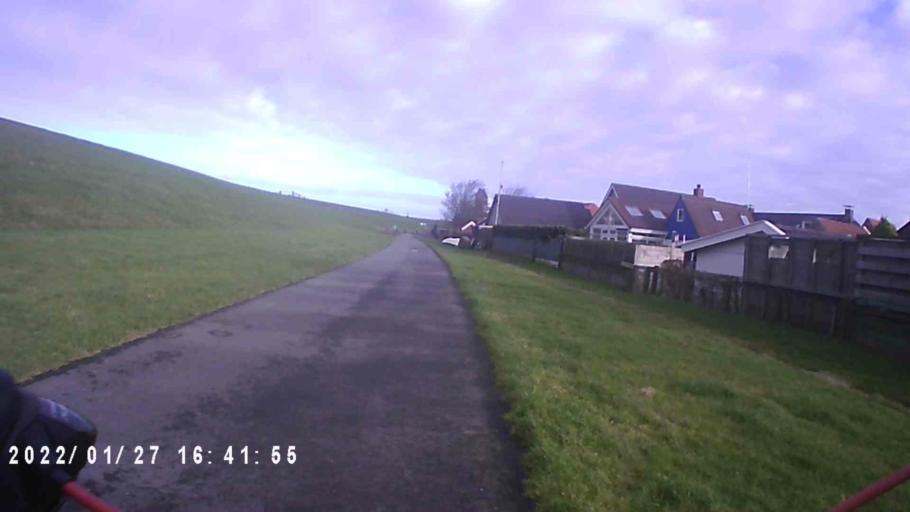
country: NL
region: Friesland
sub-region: Gemeente Dongeradeel
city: Ternaard
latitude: 53.4013
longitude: 6.0121
